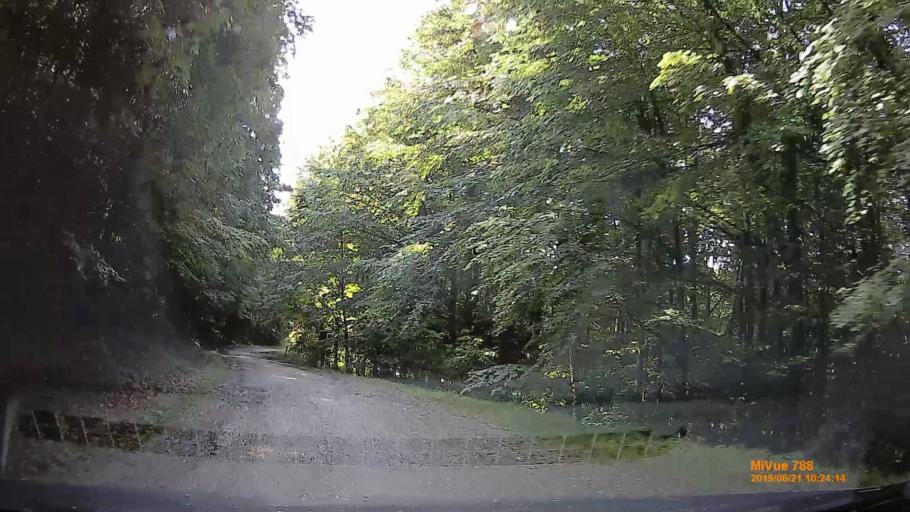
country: HU
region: Baranya
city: Buekkoesd
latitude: 46.1824
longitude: 17.9719
